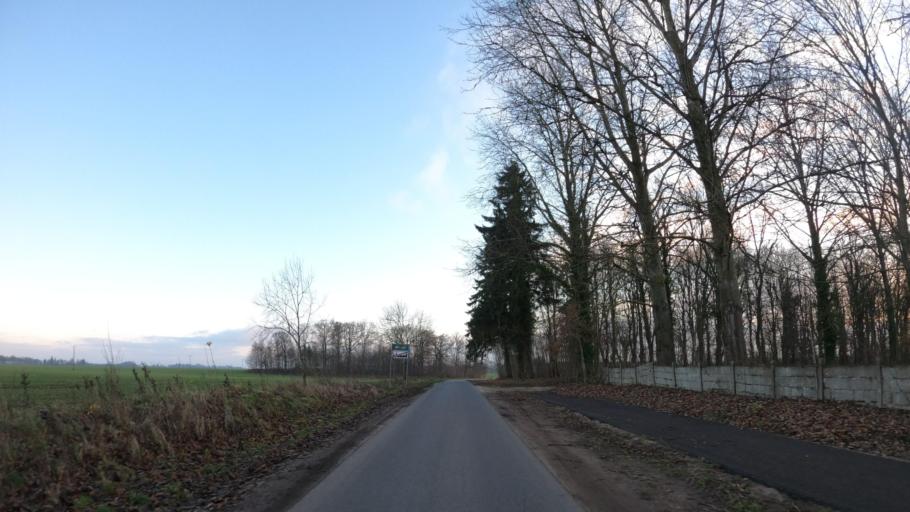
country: PL
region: West Pomeranian Voivodeship
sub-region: Powiat bialogardzki
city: Karlino
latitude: 54.1089
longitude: 15.8856
